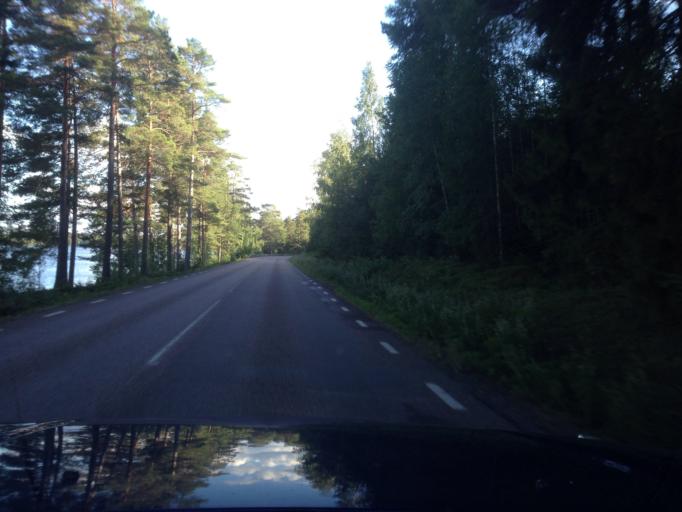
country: SE
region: Dalarna
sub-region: Ludvika Kommun
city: Grangesberg
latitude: 60.1978
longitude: 14.9668
